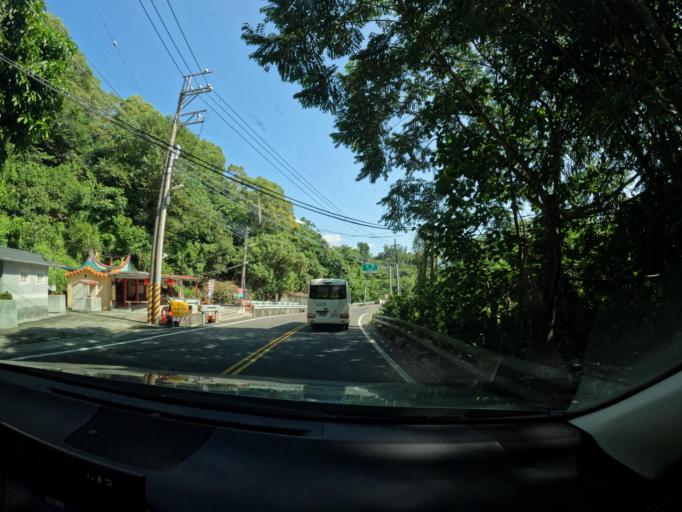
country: TW
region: Taiwan
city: Yujing
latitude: 23.0701
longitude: 120.6694
